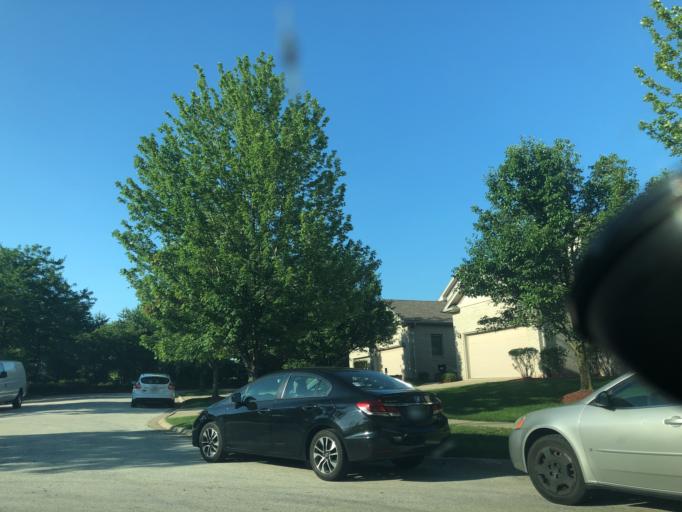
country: US
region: Illinois
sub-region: Cook County
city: Orland Hills
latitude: 41.5939
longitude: -87.8884
